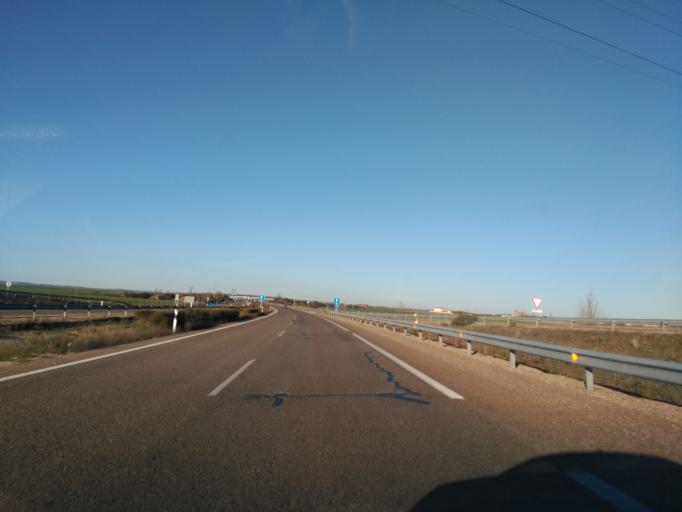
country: ES
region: Castille and Leon
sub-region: Provincia de Salamanca
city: Pedrosillo el Ralo
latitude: 41.0574
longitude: -5.5427
